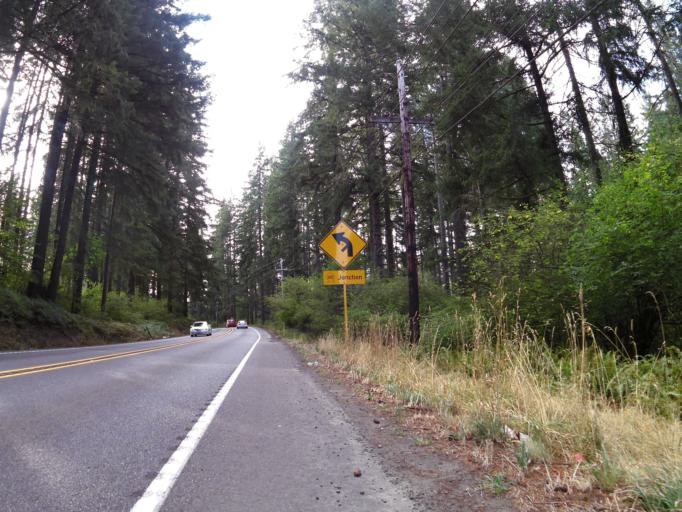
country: US
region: Washington
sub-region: Mason County
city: Allyn
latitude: 47.4135
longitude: -122.8446
